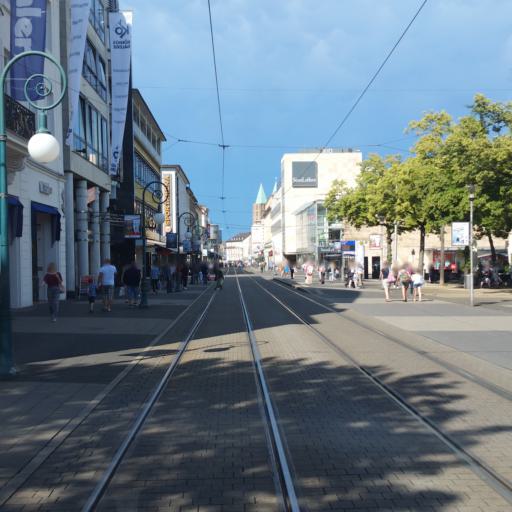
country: DE
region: Hesse
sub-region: Regierungsbezirk Kassel
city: Kassel
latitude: 51.3140
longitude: 9.4950
